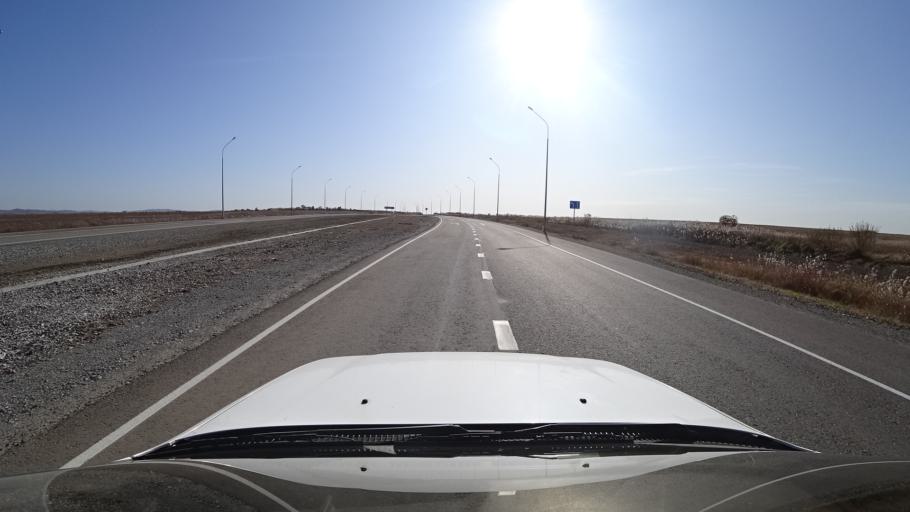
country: RU
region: Primorskiy
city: Dal'nerechensk
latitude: 45.8645
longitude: 133.7204
